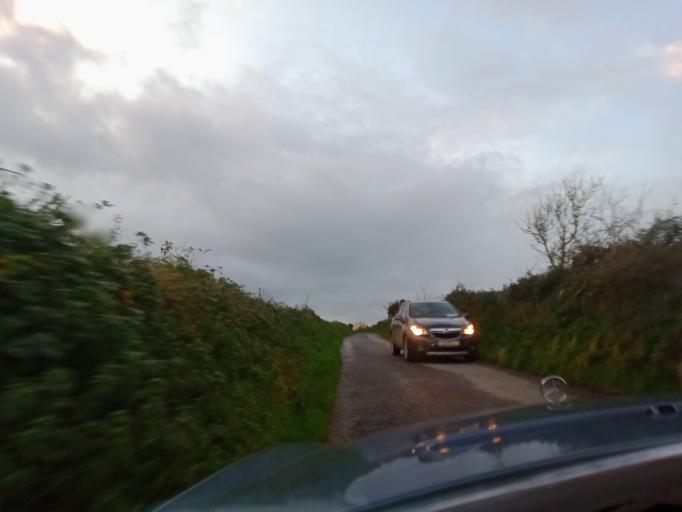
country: IE
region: Munster
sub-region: Waterford
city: Waterford
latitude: 52.3321
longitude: -7.0317
